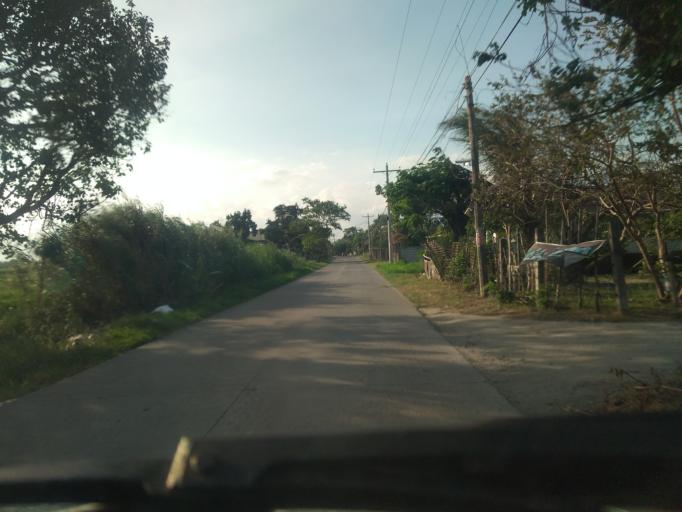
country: PH
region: Central Luzon
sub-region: Province of Pampanga
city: Bulaon
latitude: 15.0869
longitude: 120.6943
